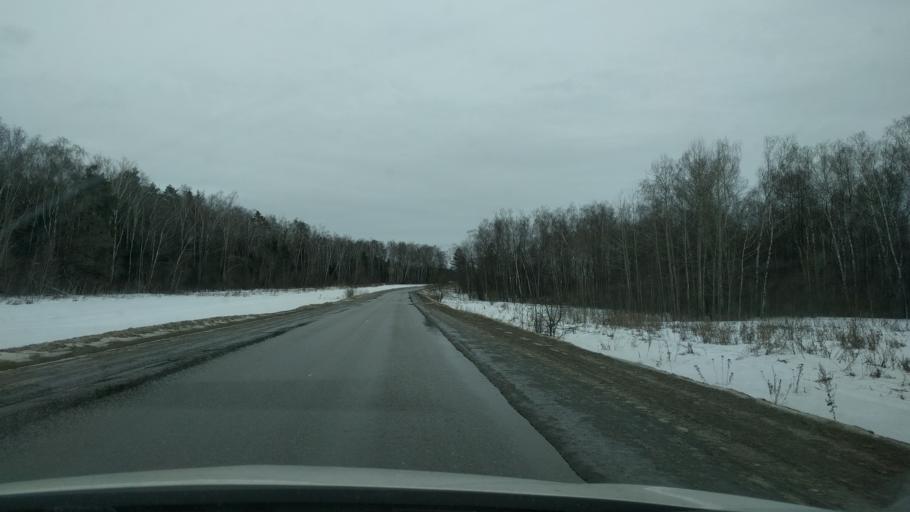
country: RU
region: Moskovskaya
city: Dubrovitsy
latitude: 55.4308
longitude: 37.4333
